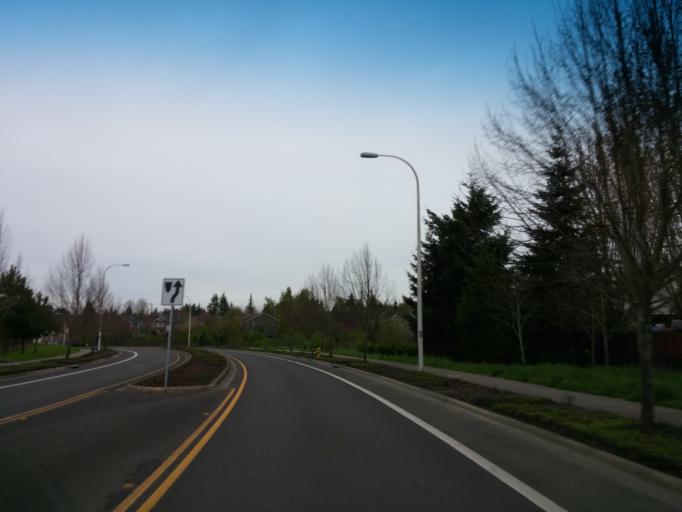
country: US
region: Oregon
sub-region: Washington County
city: Oak Hills
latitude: 45.5195
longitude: -122.8527
